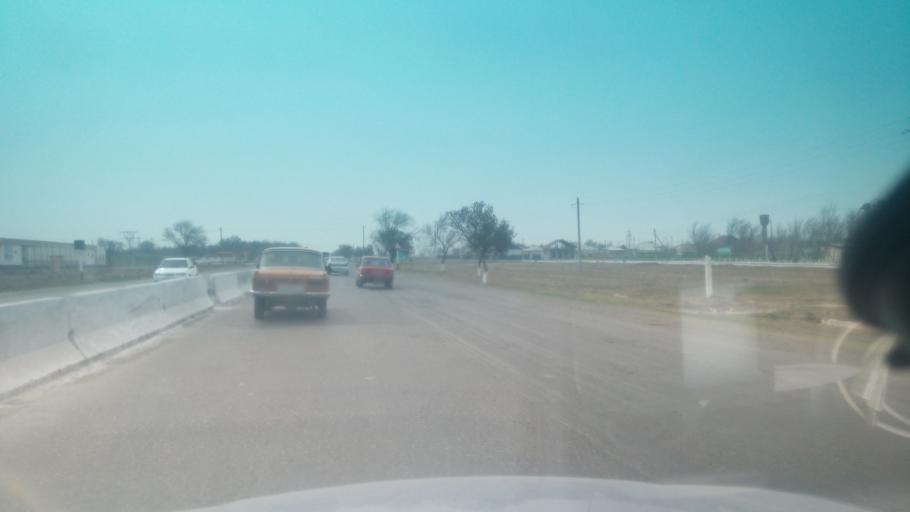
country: UZ
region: Sirdaryo
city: Yangiyer
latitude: 40.2599
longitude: 68.8329
